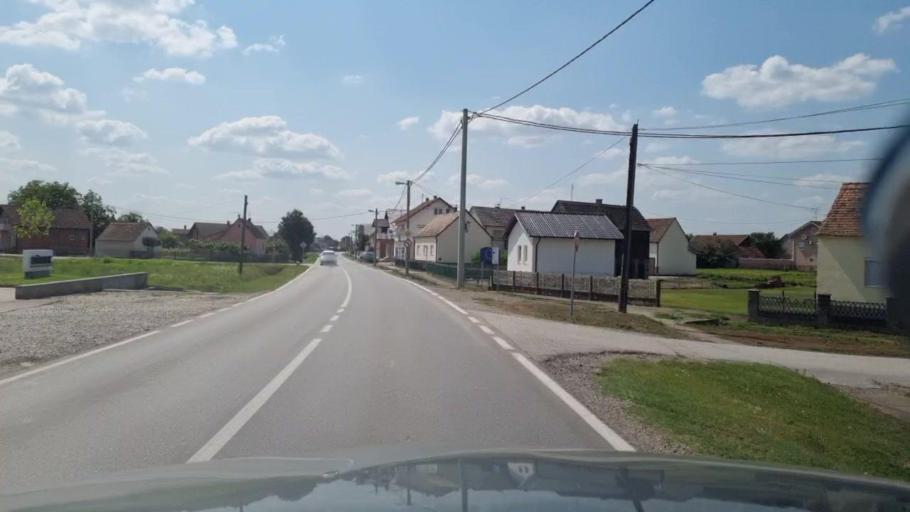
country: BA
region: Federation of Bosnia and Herzegovina
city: Donja Mahala
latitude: 45.0467
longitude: 18.6726
